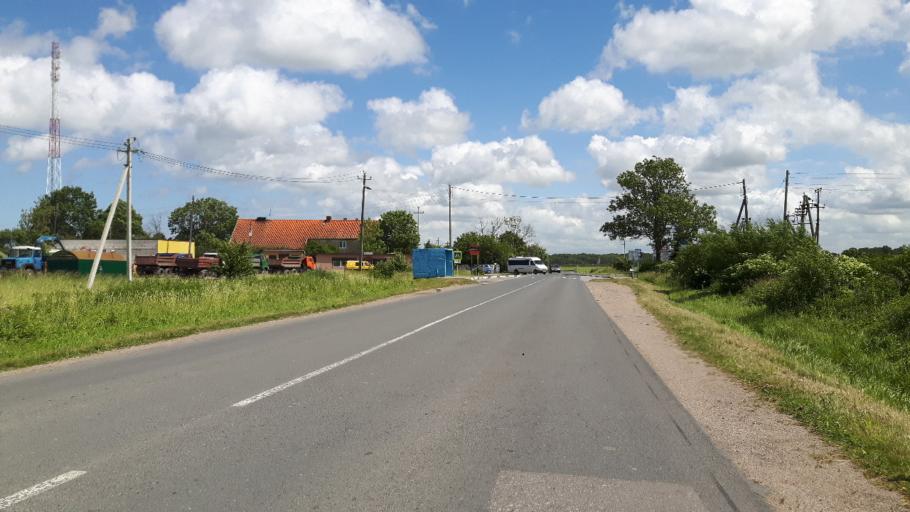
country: RU
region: Kaliningrad
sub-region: Zelenogradskiy Rayon
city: Zelenogradsk
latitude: 54.9290
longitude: 20.4164
